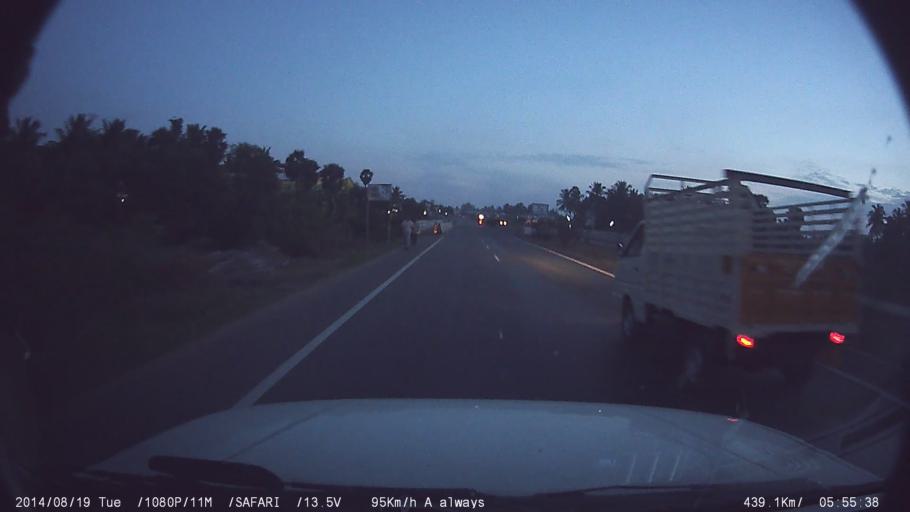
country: IN
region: Tamil Nadu
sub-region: Salem
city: Omalur
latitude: 11.7467
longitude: 78.0507
